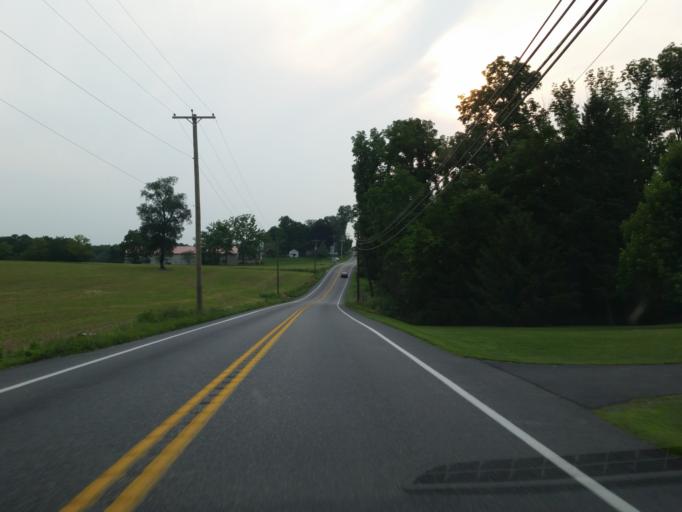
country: US
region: Pennsylvania
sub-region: Lebanon County
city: Annville
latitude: 40.3506
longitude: -76.5338
